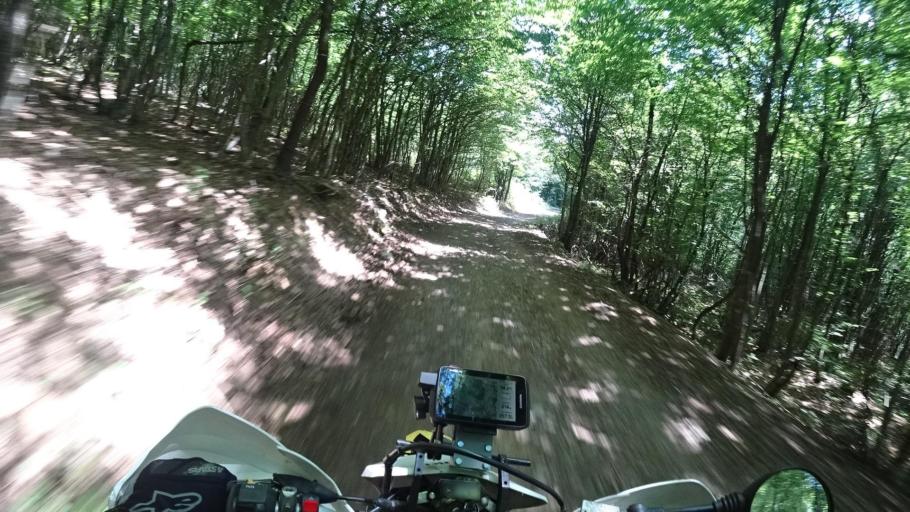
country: HR
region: Karlovacka
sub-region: Grad Ogulin
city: Ogulin
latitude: 45.3191
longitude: 15.2413
